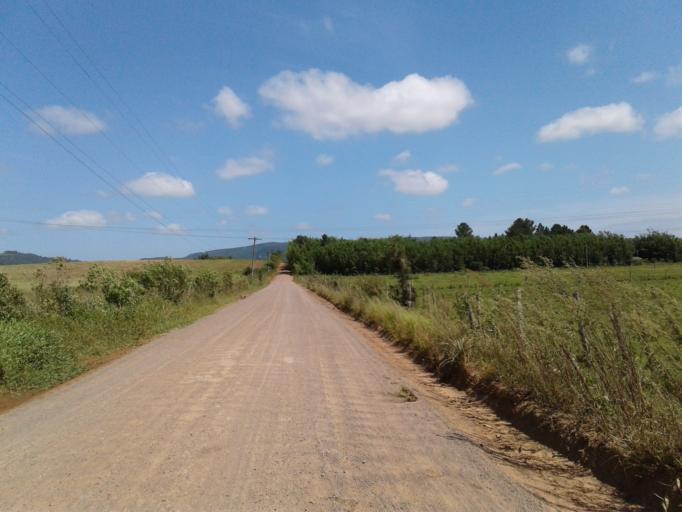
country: BR
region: Rio Grande do Sul
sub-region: Gravatai
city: Gravatai
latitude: -29.8759
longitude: -50.8199
